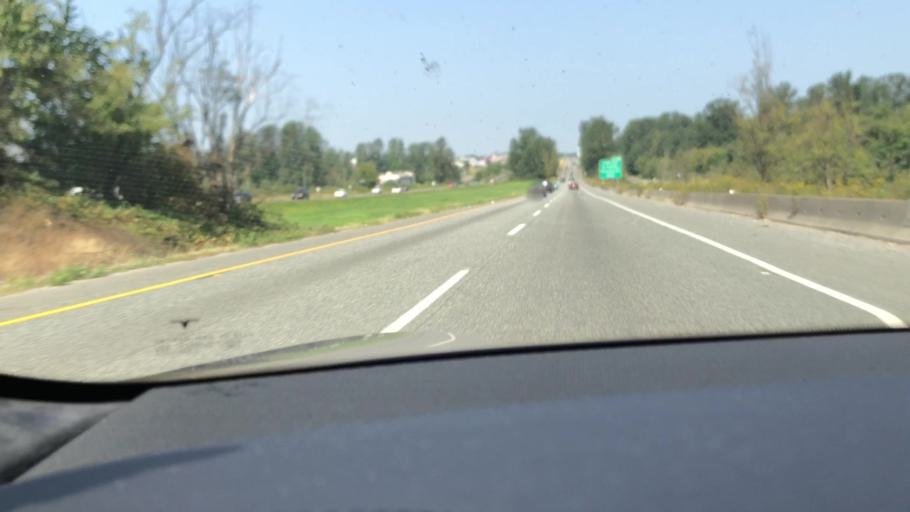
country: US
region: Washington
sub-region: Whatcom County
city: Sumas
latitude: 49.0491
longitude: -122.3605
